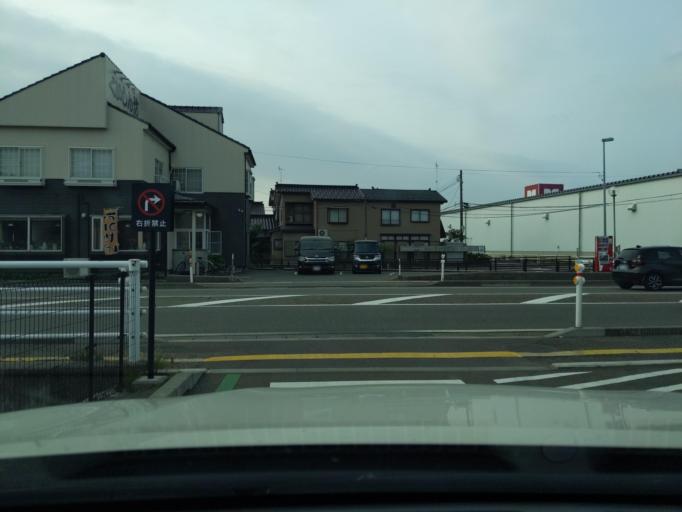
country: JP
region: Niigata
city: Kashiwazaki
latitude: 37.3608
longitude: 138.5613
